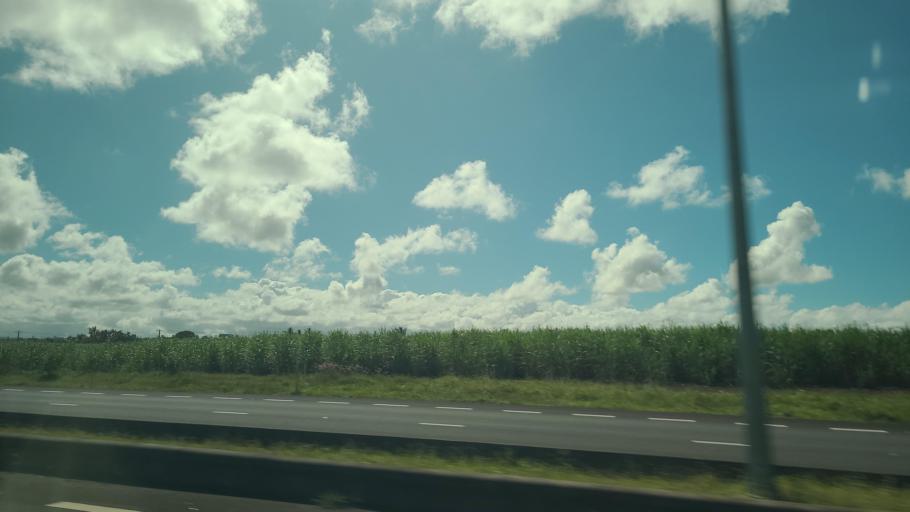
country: MU
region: Grand Port
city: Plaine Magnien
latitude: -20.4390
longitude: 57.6591
